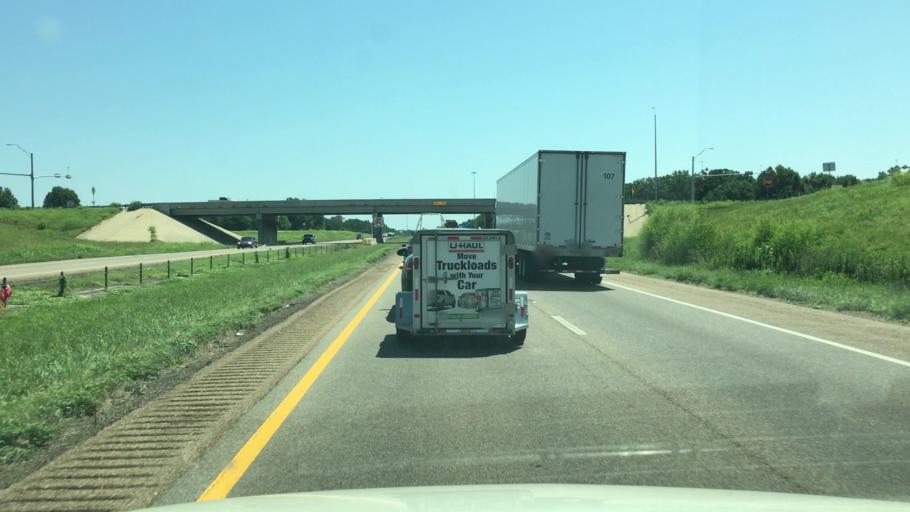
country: US
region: Texas
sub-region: Bowie County
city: Hooks
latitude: 33.4710
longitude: -94.3144
